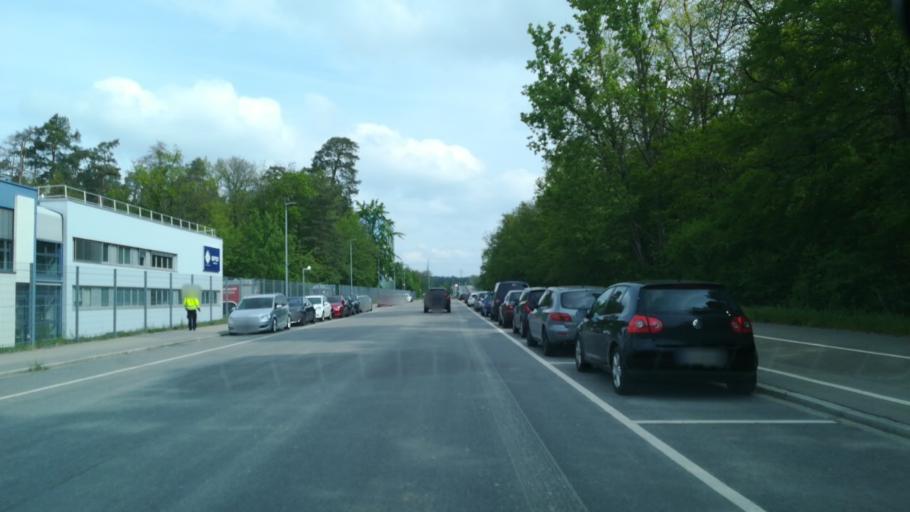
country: DE
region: Baden-Wuerttemberg
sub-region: Freiburg Region
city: Singen
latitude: 47.7545
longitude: 8.8773
